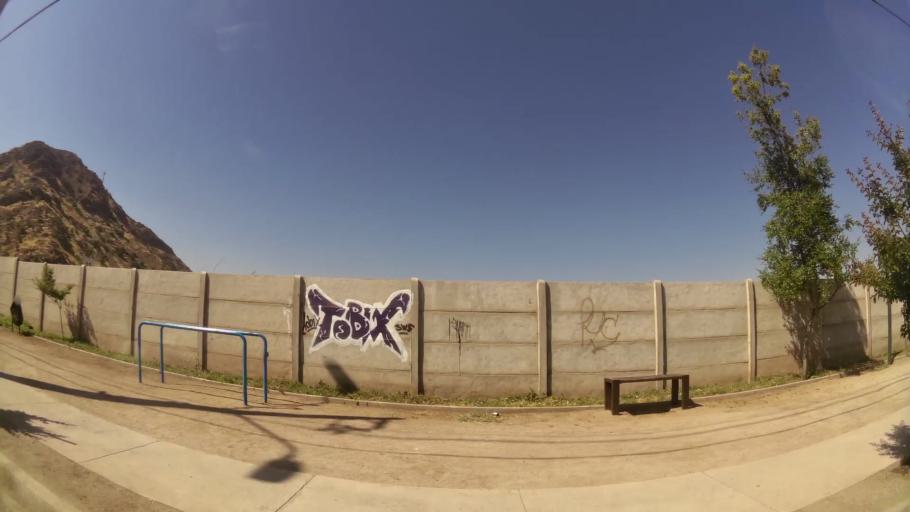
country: CL
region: Santiago Metropolitan
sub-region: Provincia de Maipo
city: San Bernardo
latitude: -33.6194
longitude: -70.6801
